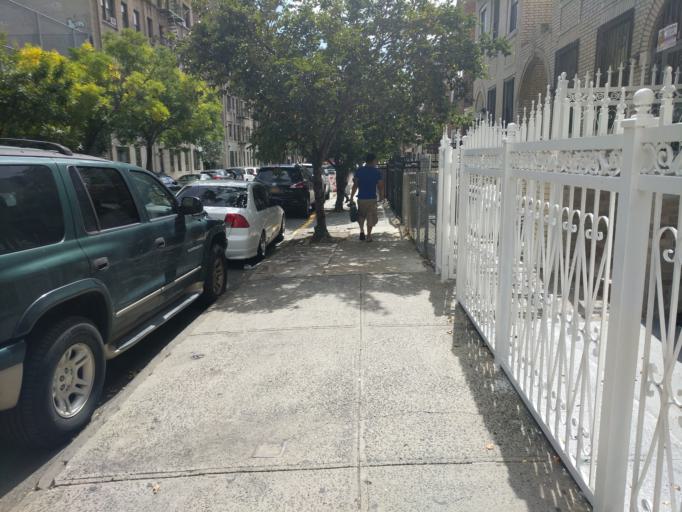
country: US
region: New York
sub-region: New York County
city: Inwood
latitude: 40.8435
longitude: -73.9214
